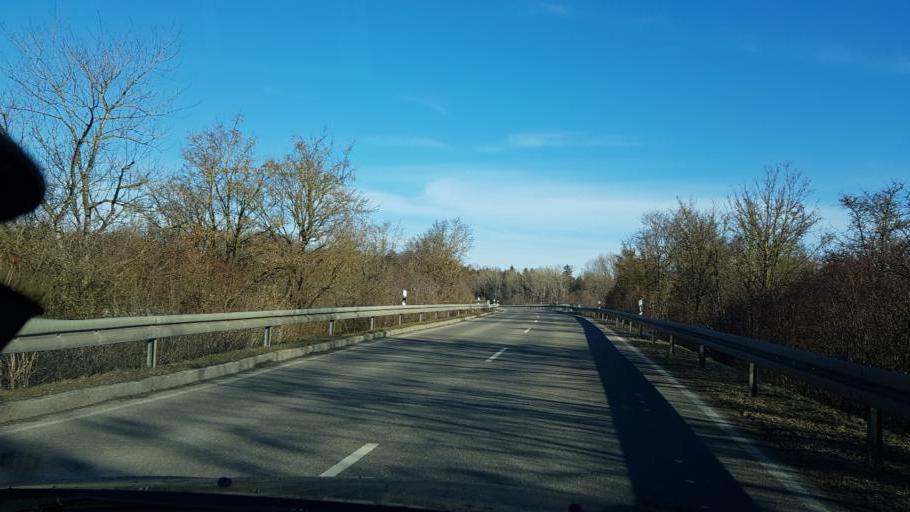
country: DE
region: Bavaria
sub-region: Upper Bavaria
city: Oberschweinbach
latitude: 48.2154
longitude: 11.1804
